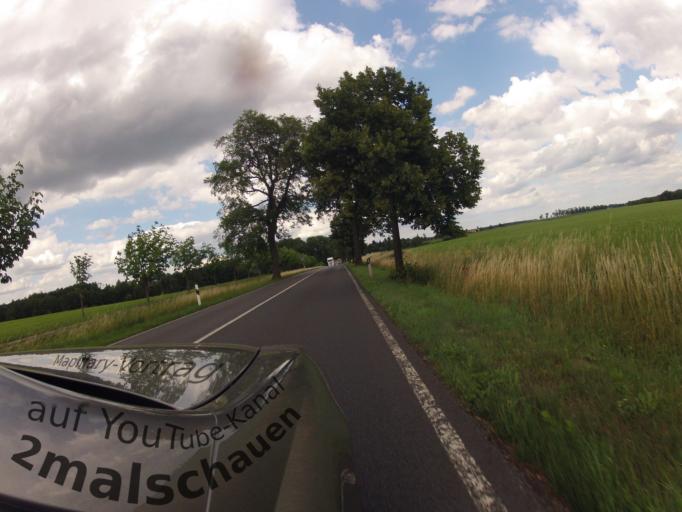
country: DE
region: Mecklenburg-Vorpommern
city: Anklam
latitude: 53.9008
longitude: 13.7368
